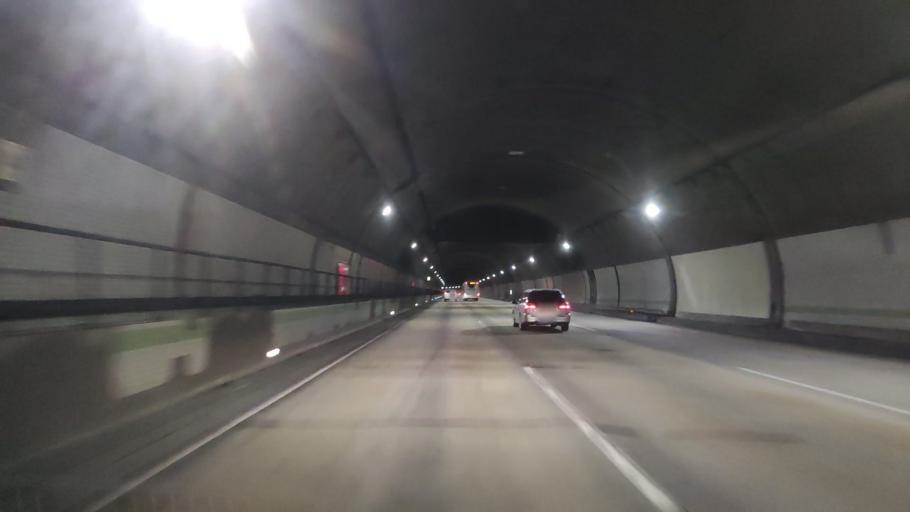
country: JP
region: Hyogo
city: Akashi
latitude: 34.6455
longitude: 135.0514
